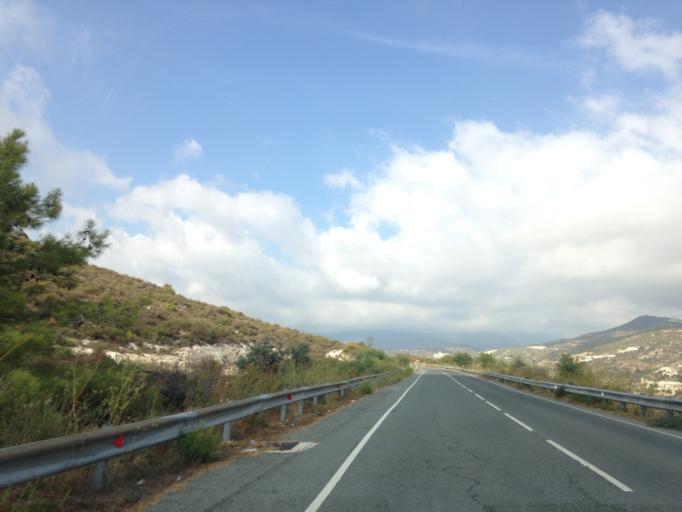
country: CY
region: Limassol
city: Pachna
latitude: 34.8306
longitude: 32.8053
